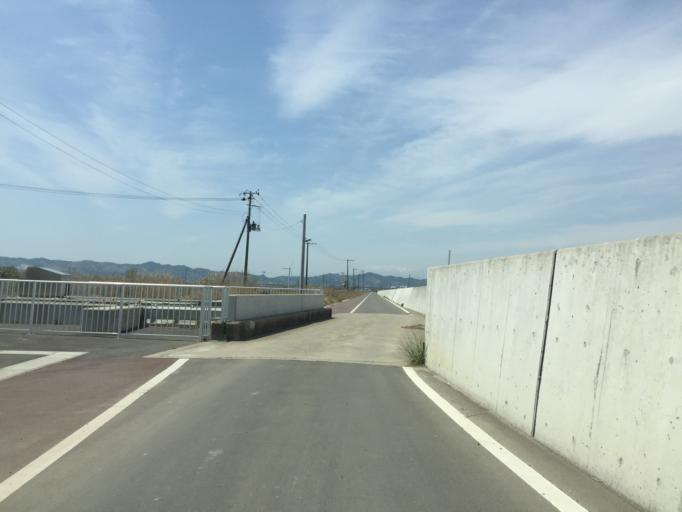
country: JP
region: Miyagi
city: Watari
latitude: 38.0312
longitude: 140.9029
